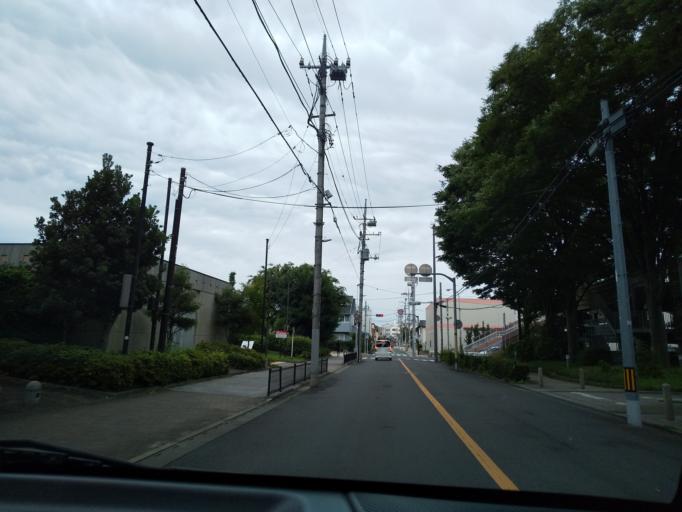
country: JP
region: Tokyo
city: Hino
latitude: 35.6674
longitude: 139.3825
